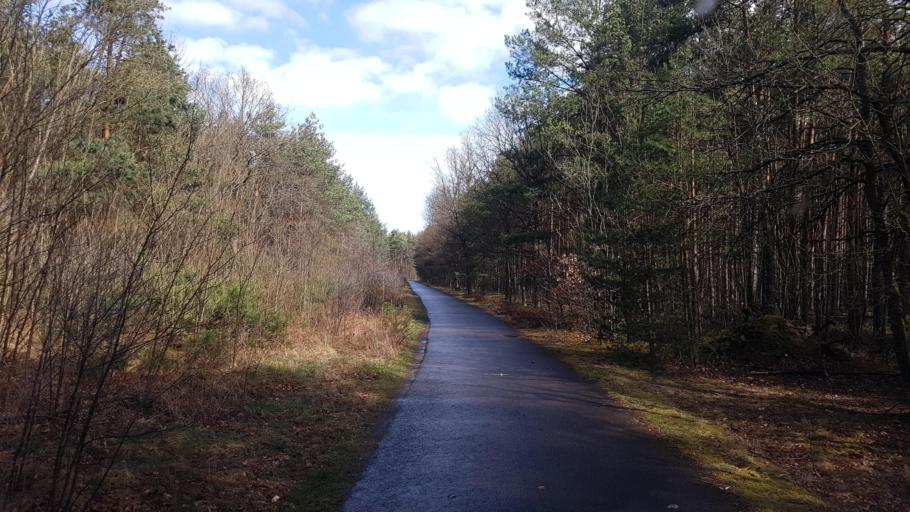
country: DE
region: Brandenburg
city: Altdobern
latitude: 51.6998
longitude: 14.0369
